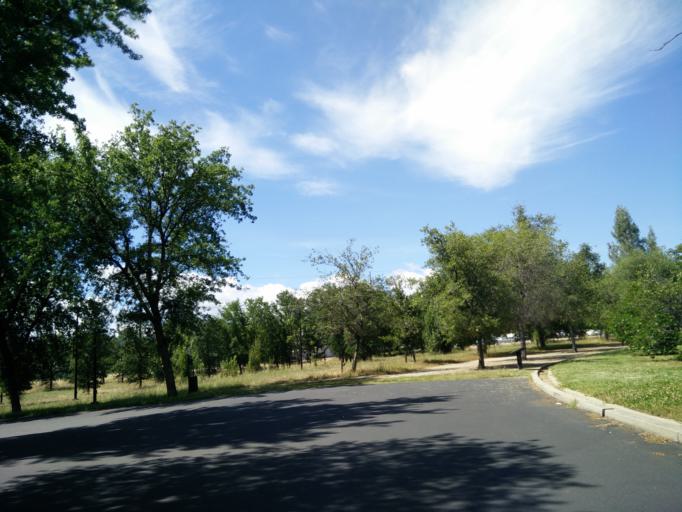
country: US
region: California
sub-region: Shasta County
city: Redding
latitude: 40.5944
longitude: -122.3865
